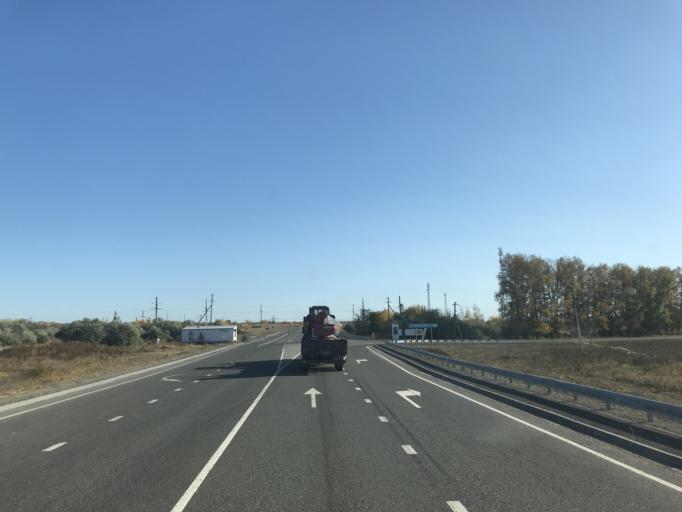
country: KZ
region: Pavlodar
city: Koktobe
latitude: 51.9269
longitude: 77.3334
